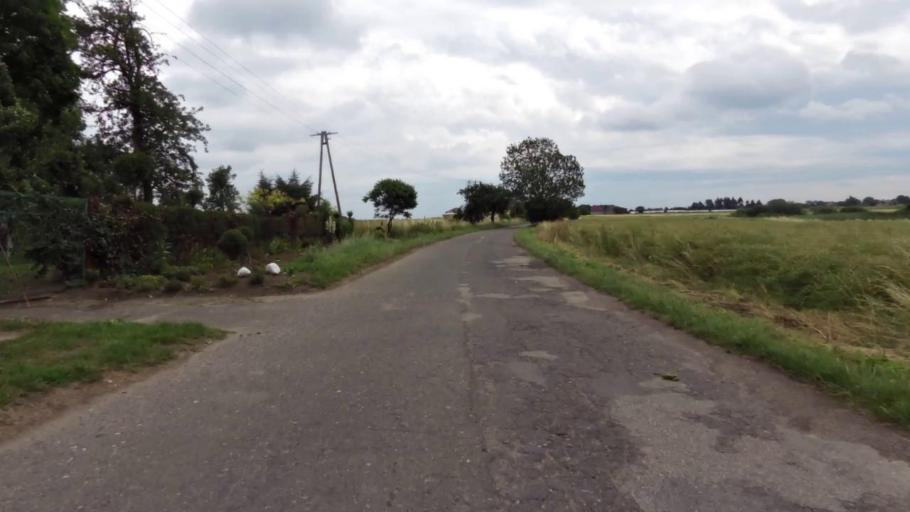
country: PL
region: West Pomeranian Voivodeship
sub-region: Powiat pyrzycki
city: Lipiany
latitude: 52.9670
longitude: 14.9446
